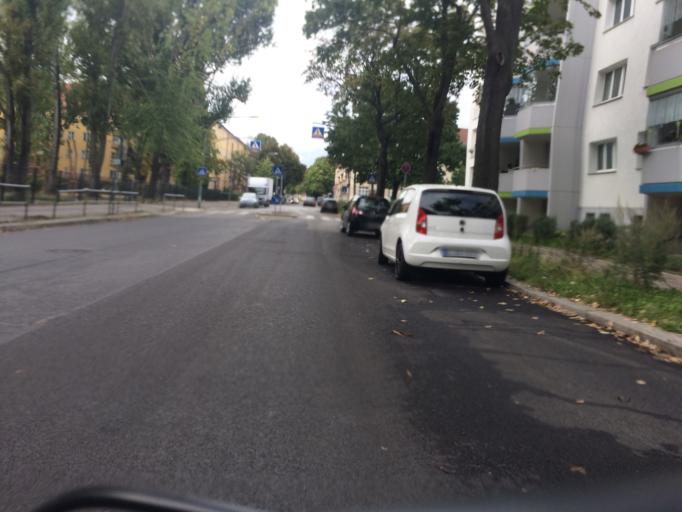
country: DE
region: Berlin
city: Alt-Hohenschoenhausen
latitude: 52.5400
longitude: 13.4960
